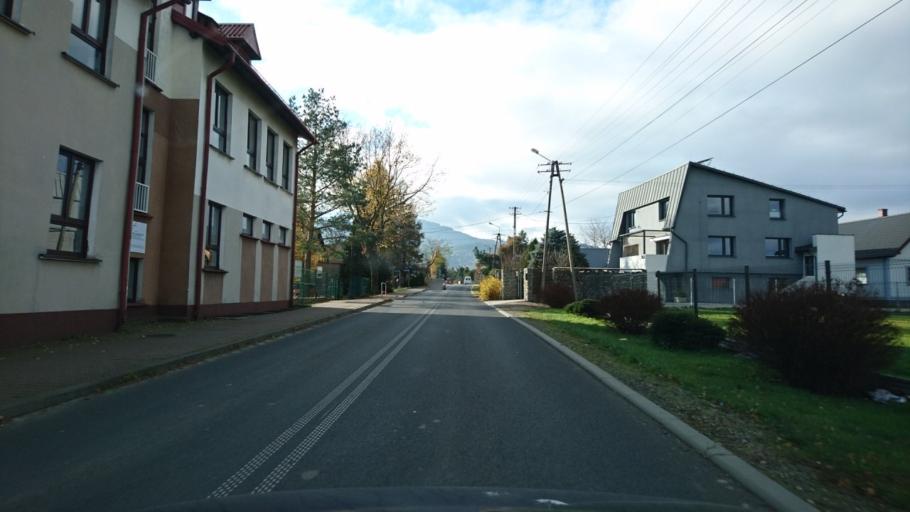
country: PL
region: Silesian Voivodeship
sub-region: Powiat bielski
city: Rybarzowice
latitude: 49.7089
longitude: 19.1042
